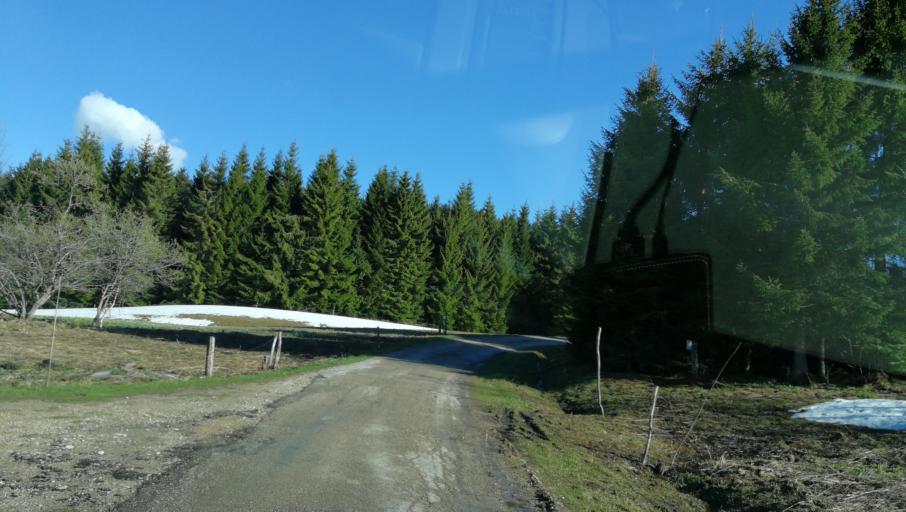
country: FR
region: Franche-Comte
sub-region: Departement du Jura
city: Saint-Claude
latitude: 46.2990
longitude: 5.8635
